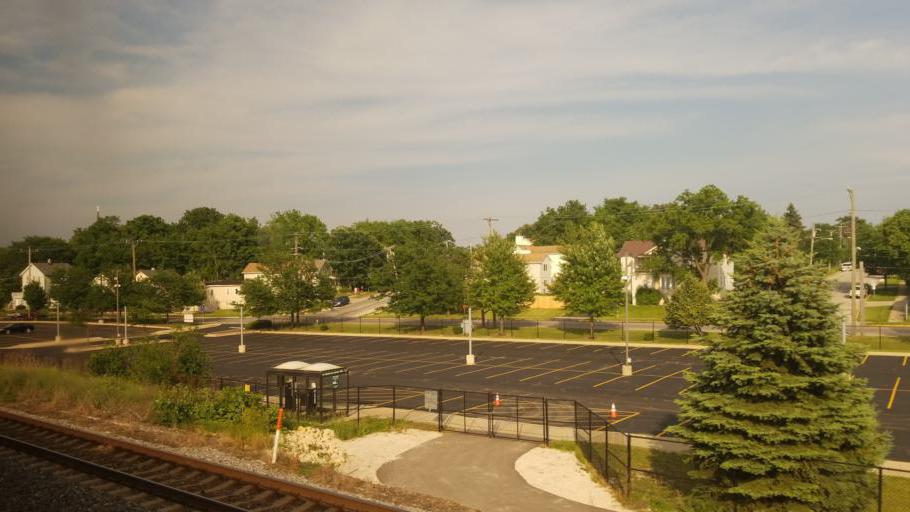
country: US
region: Illinois
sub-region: Kane County
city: Aurora
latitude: 41.7594
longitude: -88.3086
